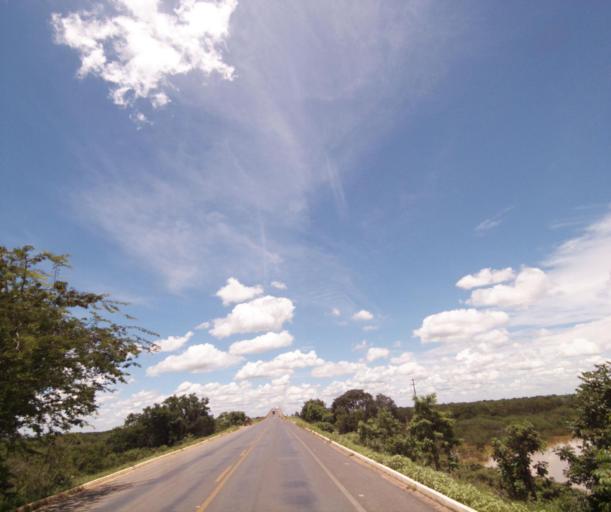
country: BR
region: Bahia
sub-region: Bom Jesus Da Lapa
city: Bom Jesus da Lapa
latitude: -13.2606
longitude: -43.4255
